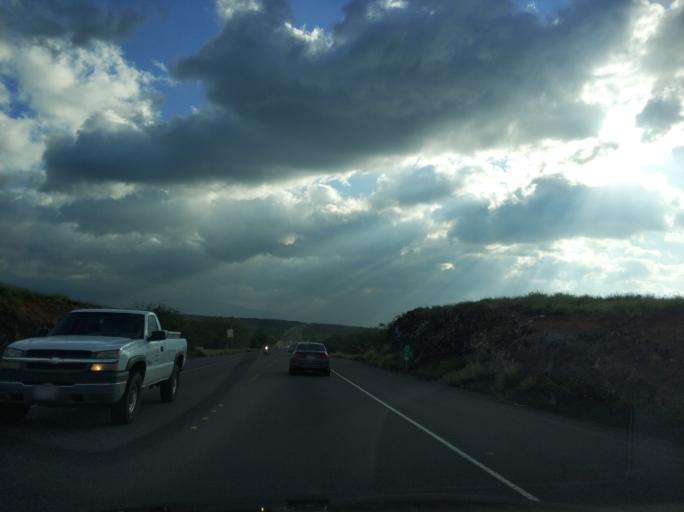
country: US
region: Hawaii
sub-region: Hawaii County
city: Waikoloa Village
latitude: 19.9532
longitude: -155.8285
